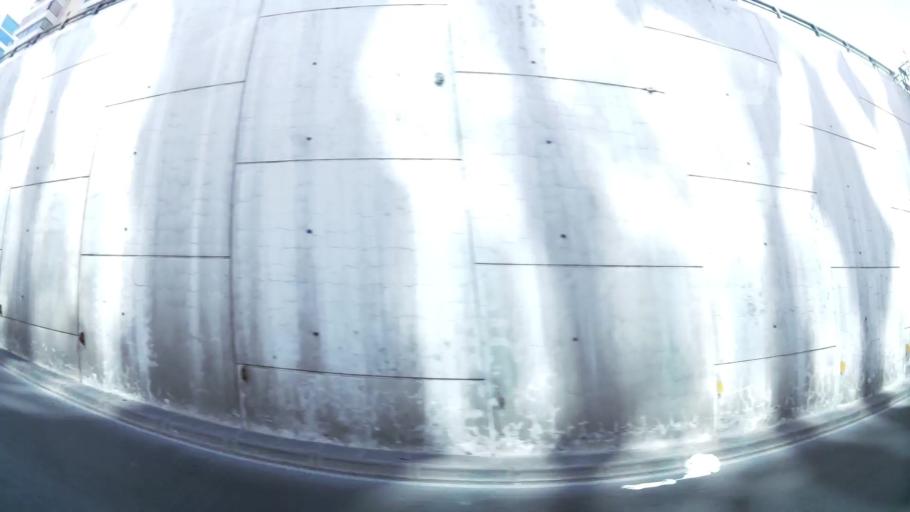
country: CL
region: Santiago Metropolitan
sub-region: Provincia de Santiago
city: Villa Presidente Frei, Nunoa, Santiago, Chile
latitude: -33.4084
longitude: -70.5670
